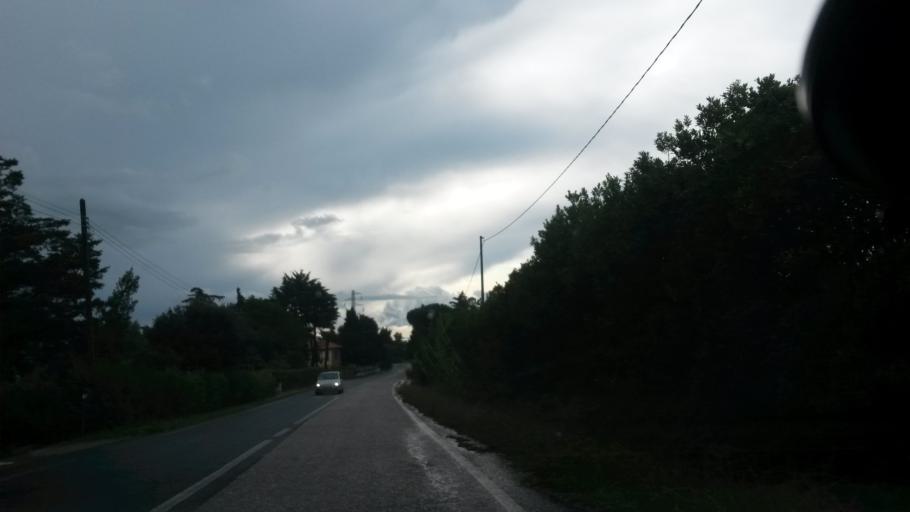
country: IT
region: Tuscany
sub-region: Provincia di Livorno
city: Rosignano Marittimo
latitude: 43.4146
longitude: 10.4517
